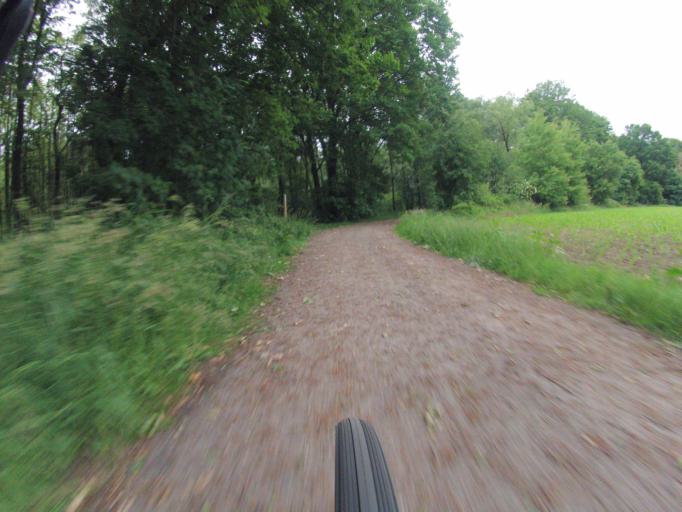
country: DE
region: North Rhine-Westphalia
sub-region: Regierungsbezirk Munster
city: Horstel
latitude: 52.2474
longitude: 7.5576
